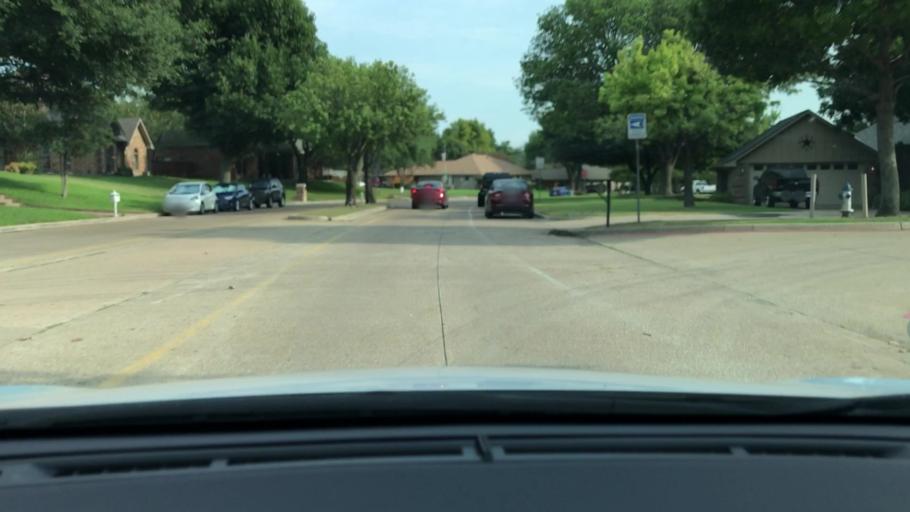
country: US
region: Texas
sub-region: Rockwall County
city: Rockwall
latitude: 32.9286
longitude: -96.4686
